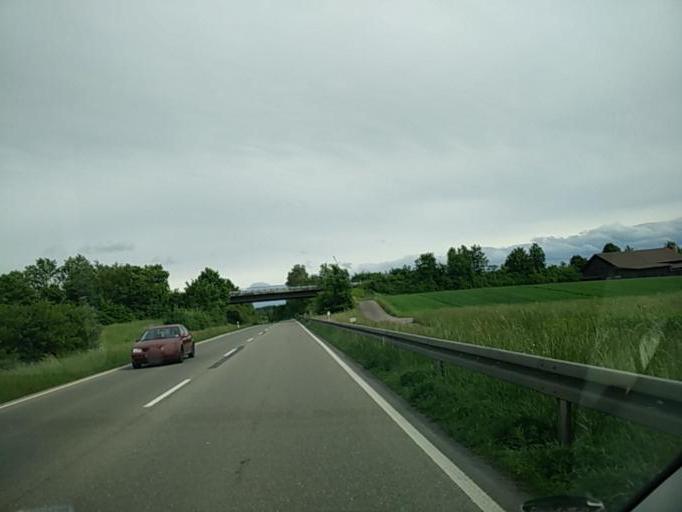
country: DE
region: Baden-Wuerttemberg
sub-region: Regierungsbezirk Stuttgart
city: Herrenberg
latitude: 48.5756
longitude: 8.9134
